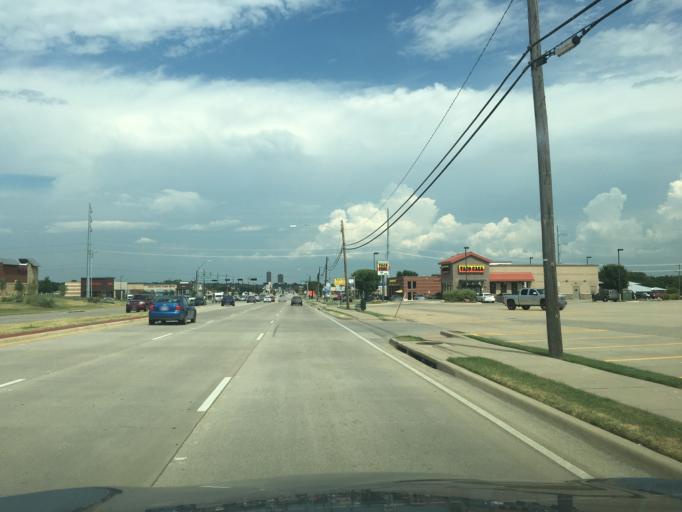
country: US
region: Texas
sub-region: Denton County
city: Denton
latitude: 33.2297
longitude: -97.1629
